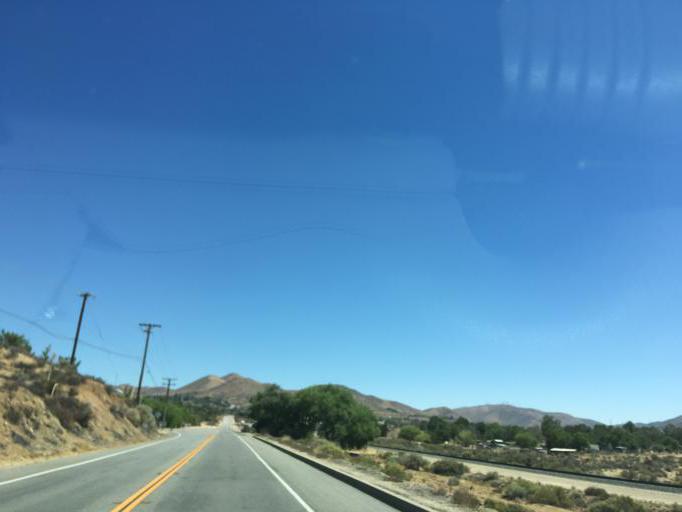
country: US
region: California
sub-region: Los Angeles County
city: Acton
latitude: 34.4730
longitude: -118.1739
